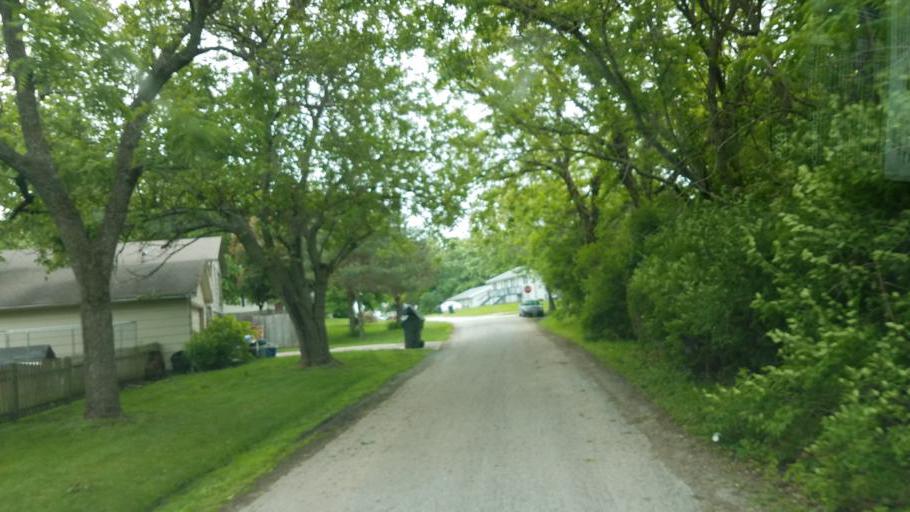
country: US
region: Iowa
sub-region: Decatur County
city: Lamoni
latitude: 40.6203
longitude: -93.9263
